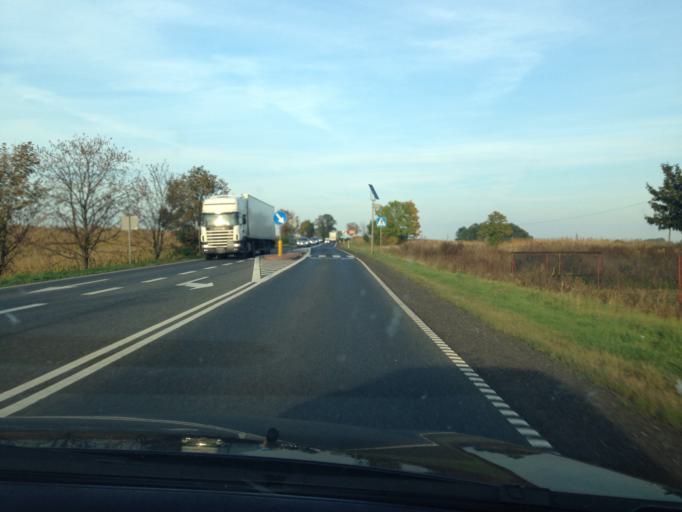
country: PL
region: Greater Poland Voivodeship
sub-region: Powiat gnieznienski
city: Trzemeszno
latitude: 52.5683
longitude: 17.8420
